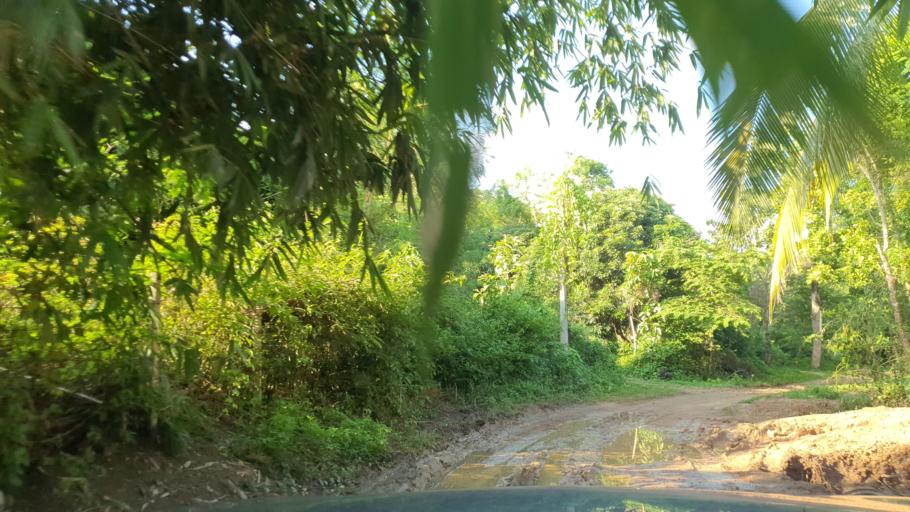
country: TH
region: Chiang Mai
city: Hang Dong
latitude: 18.7110
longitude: 98.8578
